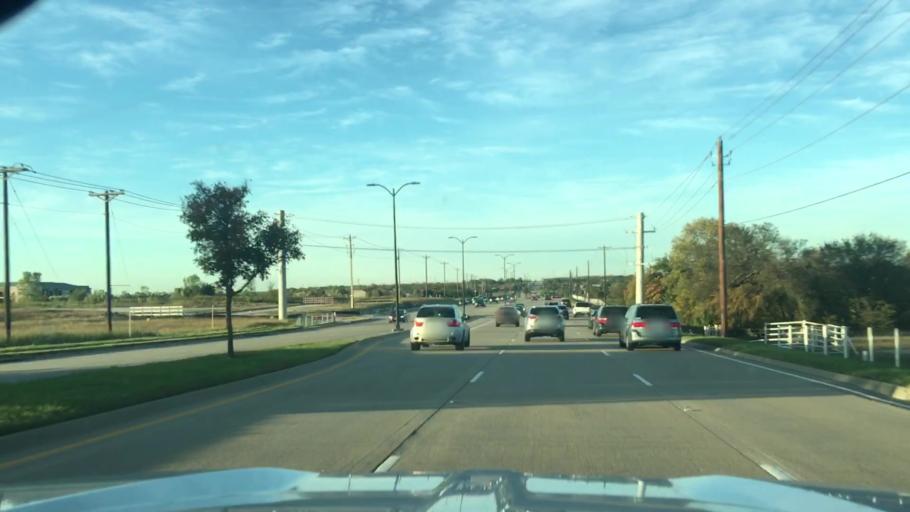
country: US
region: Texas
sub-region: Collin County
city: Frisco
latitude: 33.1697
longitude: -96.8030
